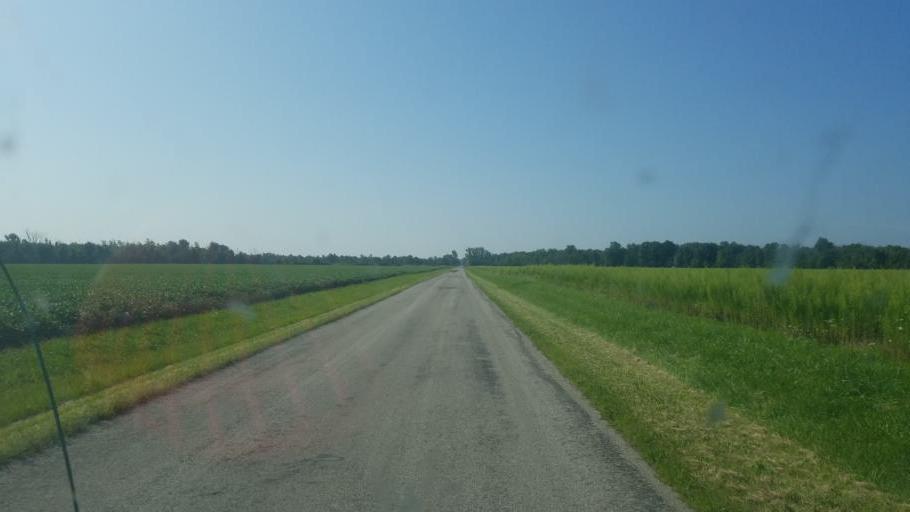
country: US
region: Ohio
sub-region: Lorain County
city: Wellington
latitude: 41.0988
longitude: -82.2007
